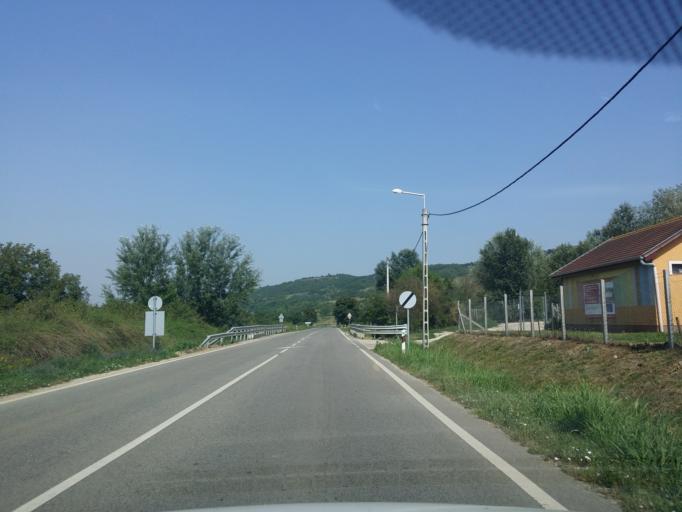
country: HU
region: Tolna
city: Pincehely
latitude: 46.6940
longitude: 18.4583
